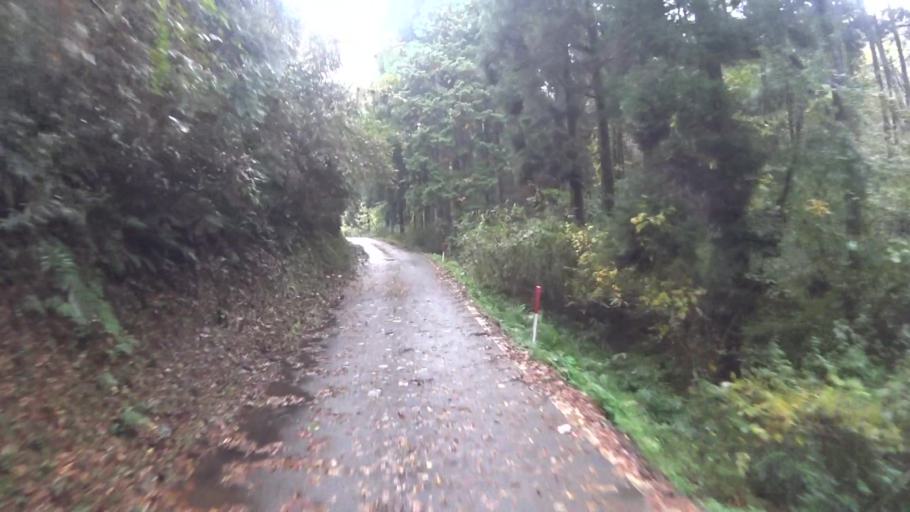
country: JP
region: Kyoto
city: Ayabe
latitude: 35.2613
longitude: 135.2227
